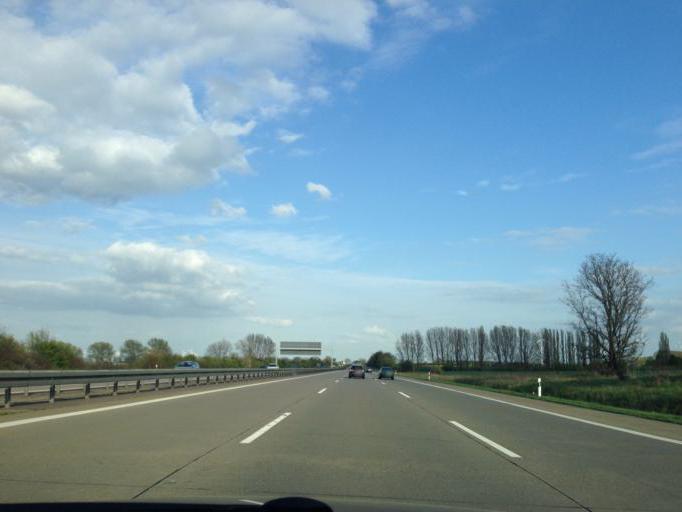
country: DE
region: Saxony-Anhalt
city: Erxleben
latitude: 52.1943
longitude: 11.2815
